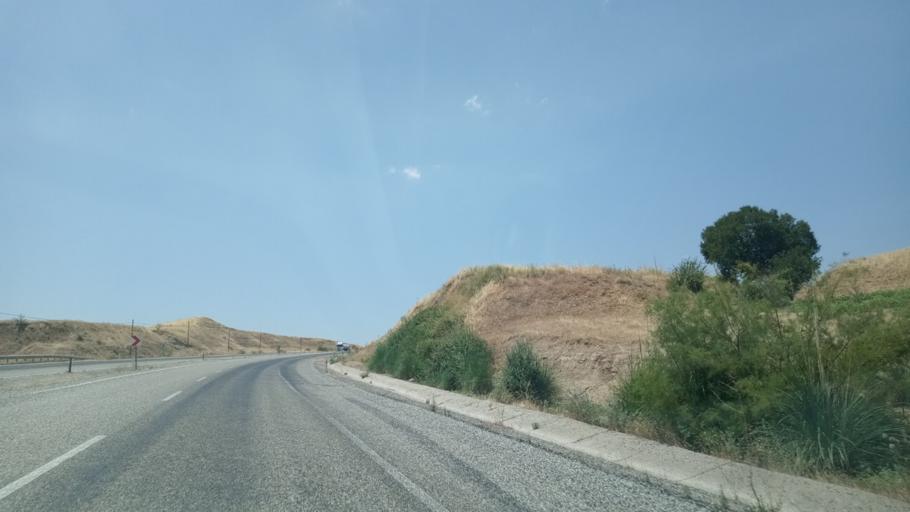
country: TR
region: Batman
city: Bekirhan
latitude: 38.1369
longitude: 41.2734
